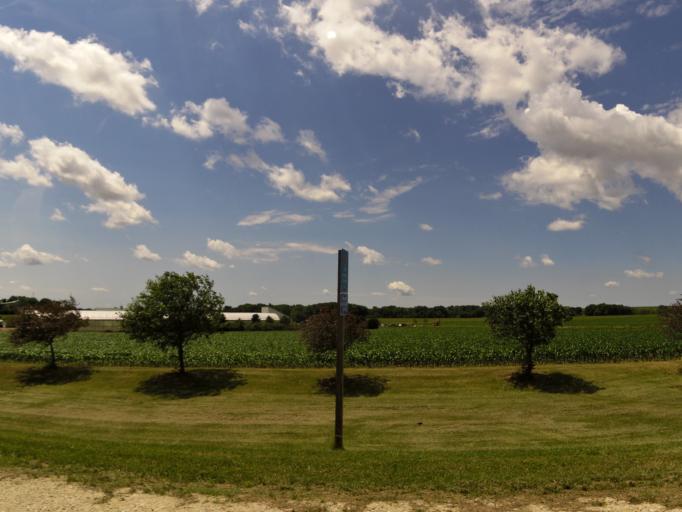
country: US
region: Iowa
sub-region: Fayette County
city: Oelwein
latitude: 42.7145
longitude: -91.9138
